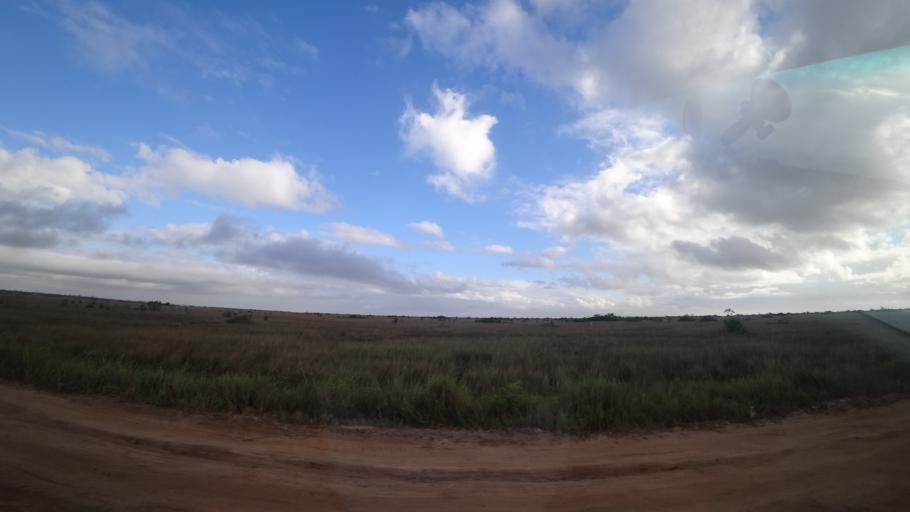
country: MZ
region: Sofala
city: Beira
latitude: -19.7054
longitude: 35.0197
